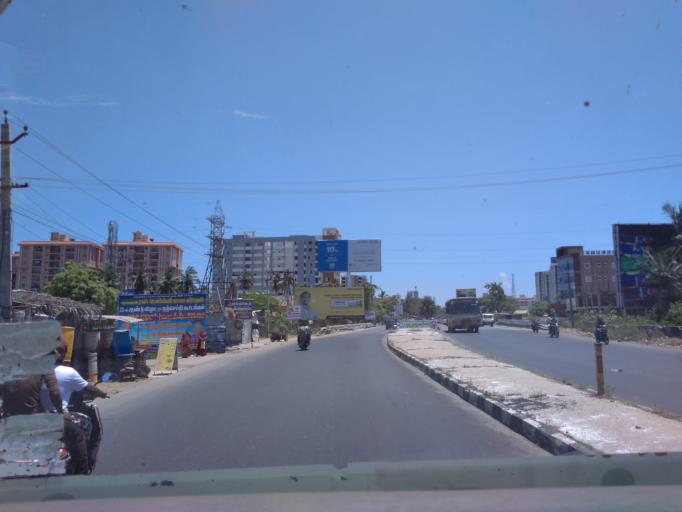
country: IN
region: Tamil Nadu
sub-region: Kancheepuram
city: Injambakkam
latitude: 12.8251
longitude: 80.2313
